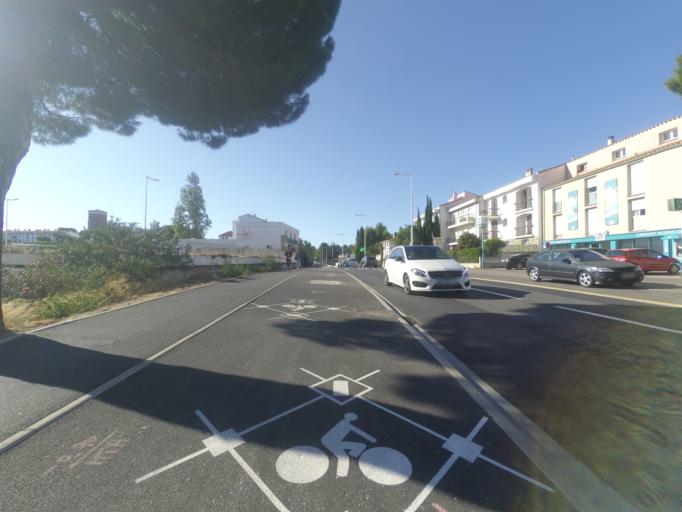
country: FR
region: Languedoc-Roussillon
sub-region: Departement des Pyrenees-Orientales
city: Perpignan
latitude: 42.6845
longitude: 2.9019
